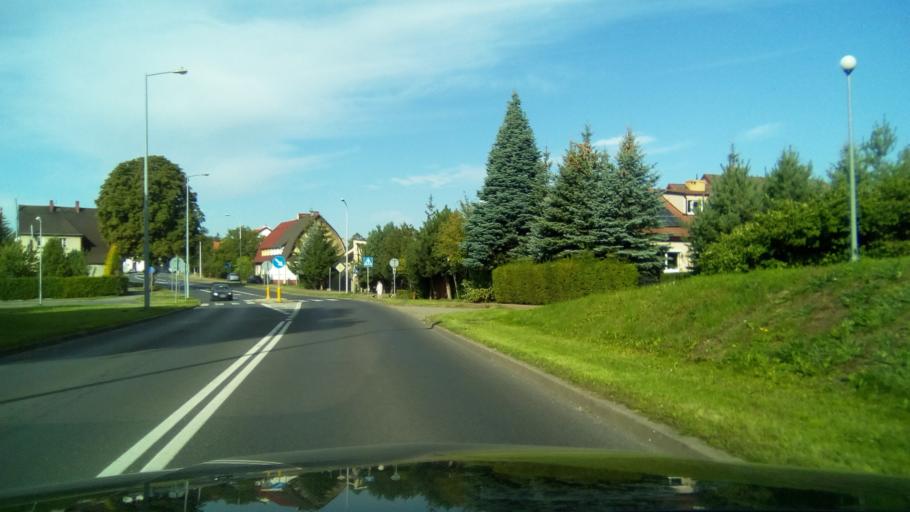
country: PL
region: Greater Poland Voivodeship
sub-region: Powiat pilski
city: Pila
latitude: 53.1426
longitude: 16.7203
